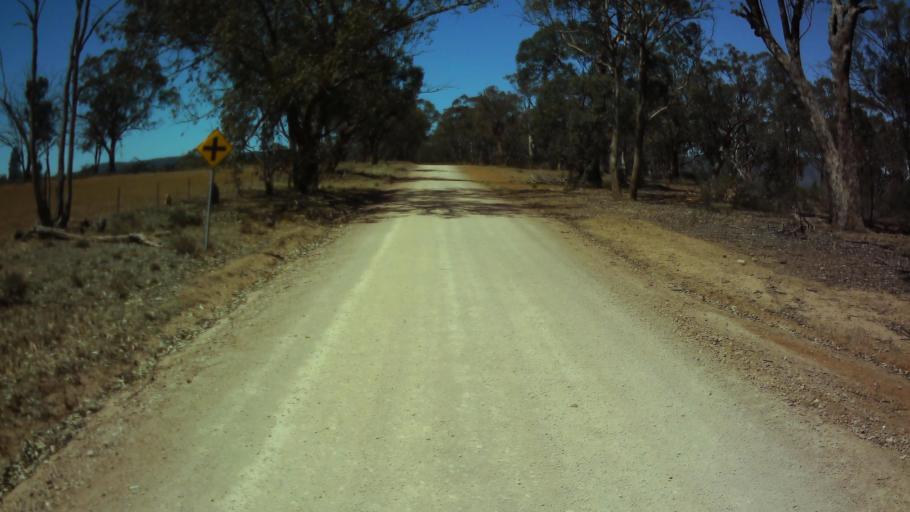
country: AU
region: New South Wales
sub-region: Weddin
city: Grenfell
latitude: -33.9306
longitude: 148.0776
